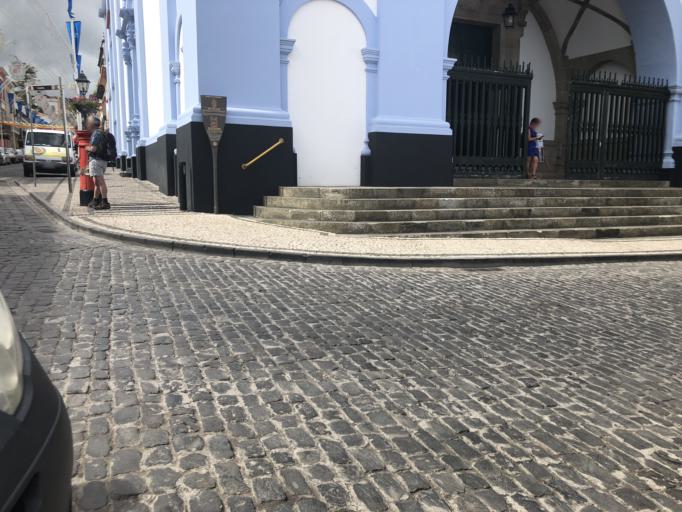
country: PT
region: Azores
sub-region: Angra do Heroismo
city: Angra do Heroismo
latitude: 38.6540
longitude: -27.2184
